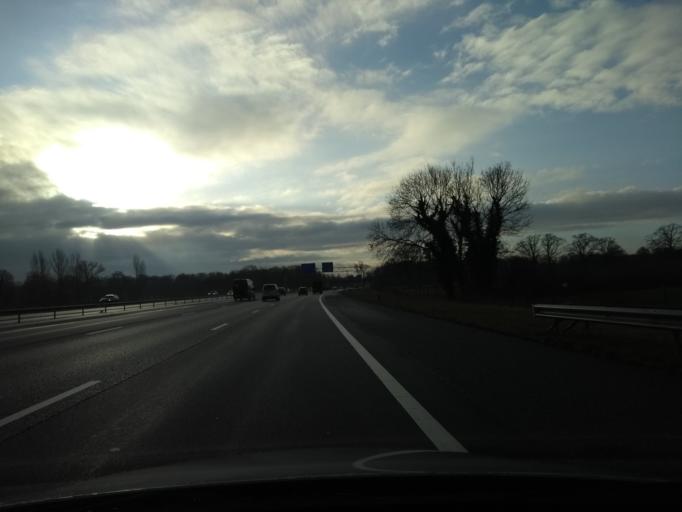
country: NL
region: Overijssel
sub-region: Gemeente Borne
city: Borne
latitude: 52.2619
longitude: 6.7513
